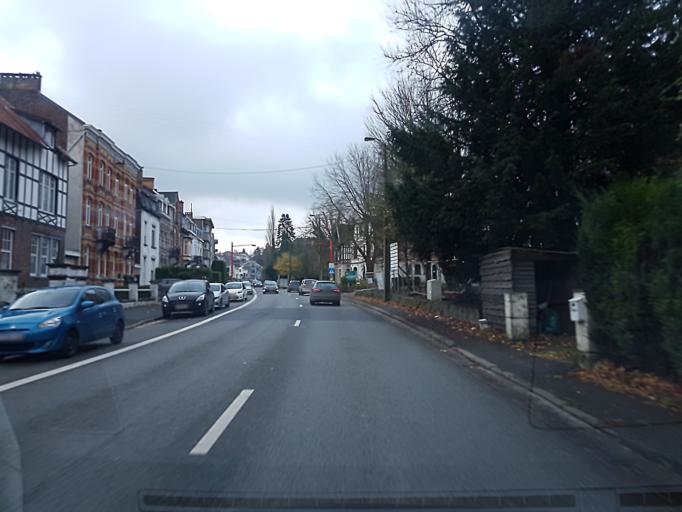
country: BE
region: Wallonia
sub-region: Province de Liege
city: Verviers
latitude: 50.5736
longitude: 5.8662
